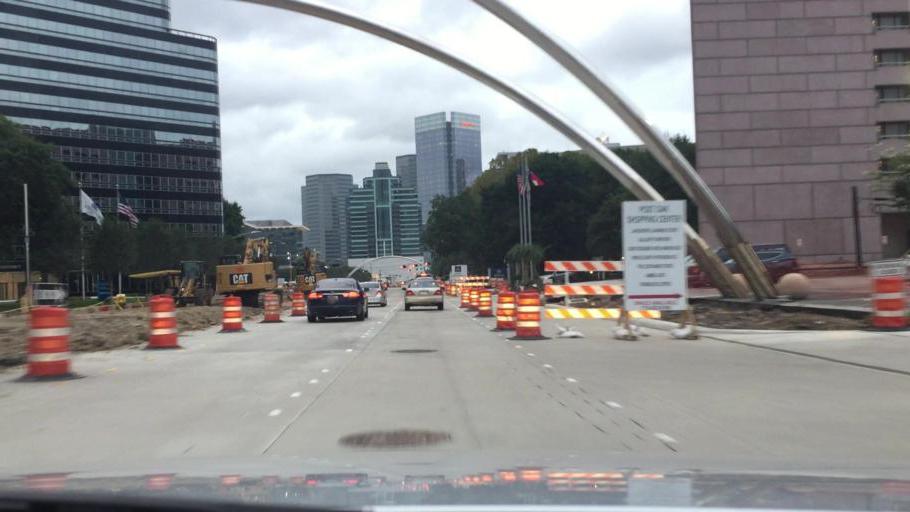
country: US
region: Texas
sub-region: Harris County
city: West University Place
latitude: 29.7449
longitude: -95.4610
